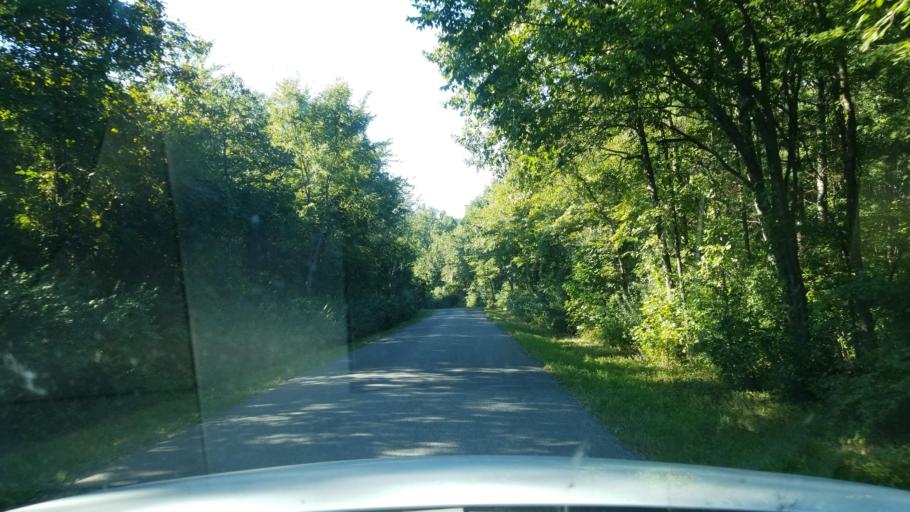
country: US
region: Illinois
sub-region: Hardin County
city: Elizabethtown
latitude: 37.5999
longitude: -88.3726
